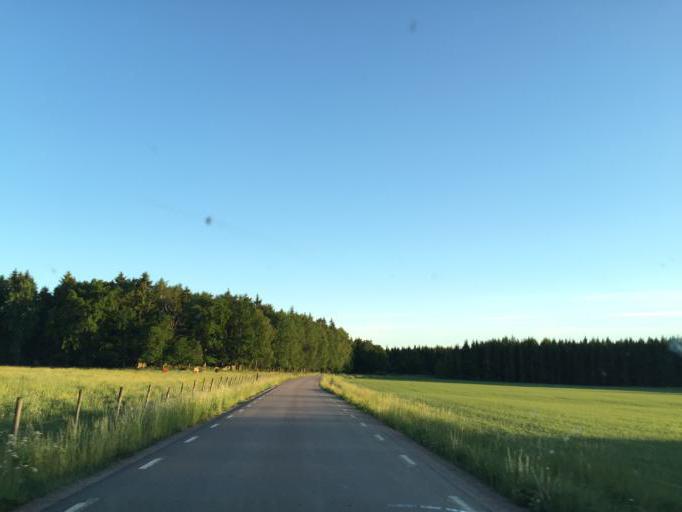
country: SE
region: Soedermanland
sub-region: Eskilstuna Kommun
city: Kvicksund
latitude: 59.5018
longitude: 16.3712
